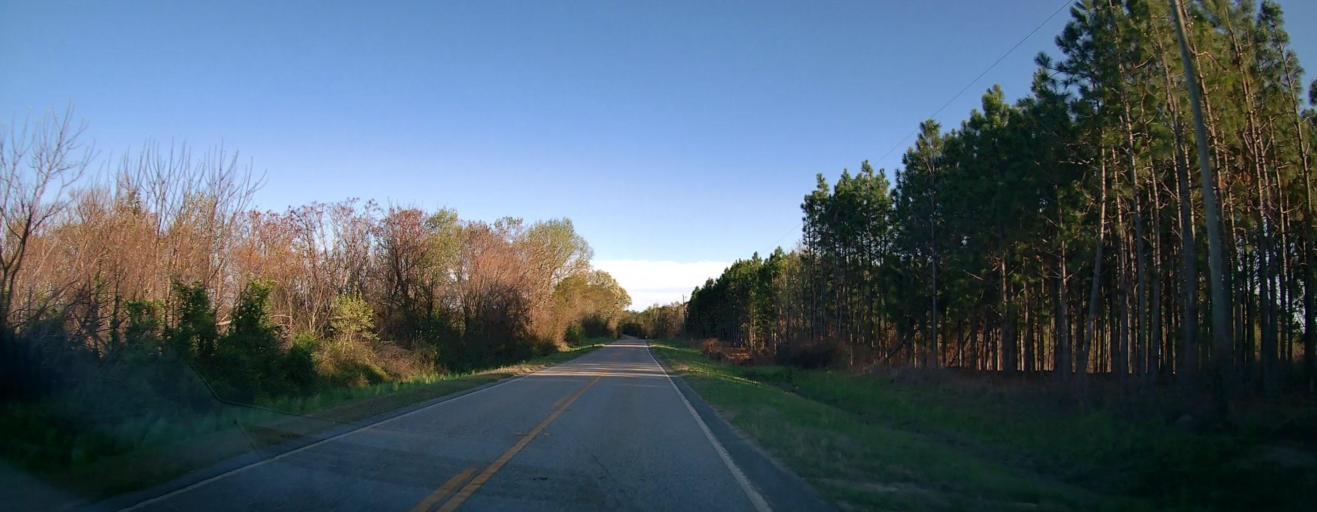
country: US
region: Georgia
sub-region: Wilcox County
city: Abbeville
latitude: 32.1148
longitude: -83.3218
